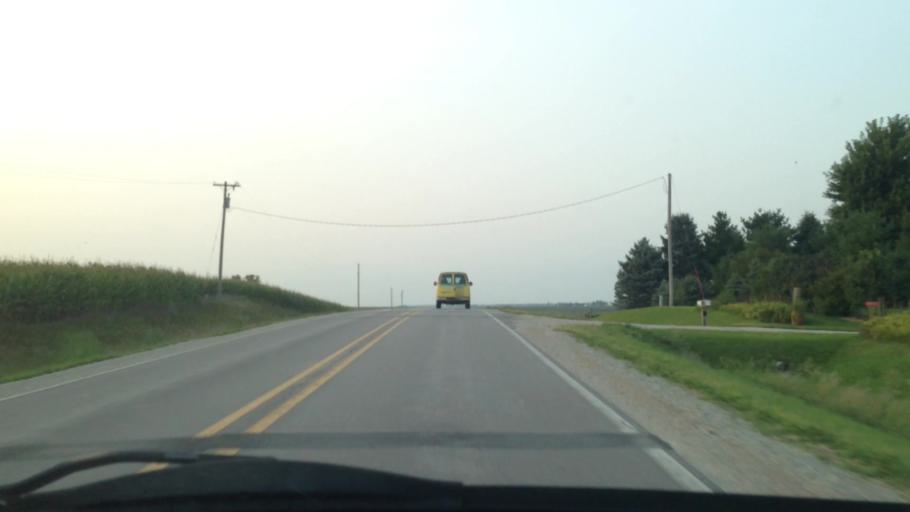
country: US
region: Iowa
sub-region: Benton County
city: Atkins
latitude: 42.0219
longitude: -91.8739
